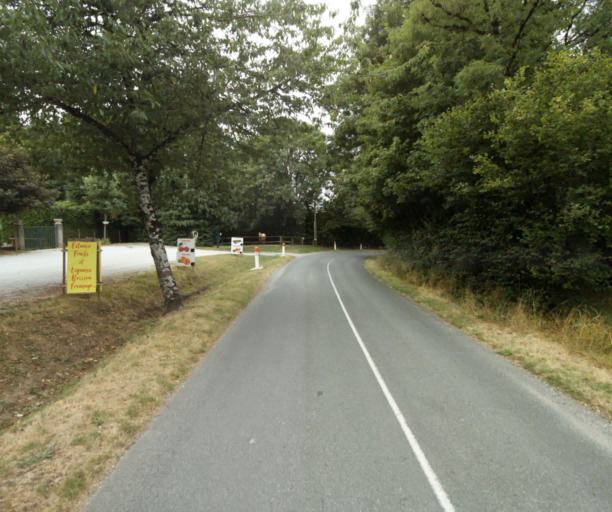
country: FR
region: Midi-Pyrenees
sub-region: Departement du Tarn
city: Soreze
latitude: 43.4072
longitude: 2.0818
